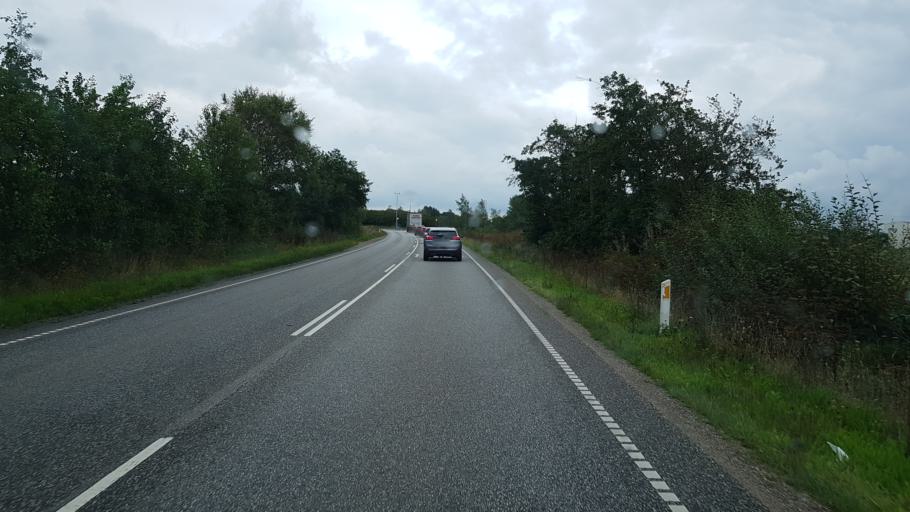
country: DK
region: Central Jutland
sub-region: Horsens Kommune
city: Horsens
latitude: 55.8885
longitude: 9.7748
